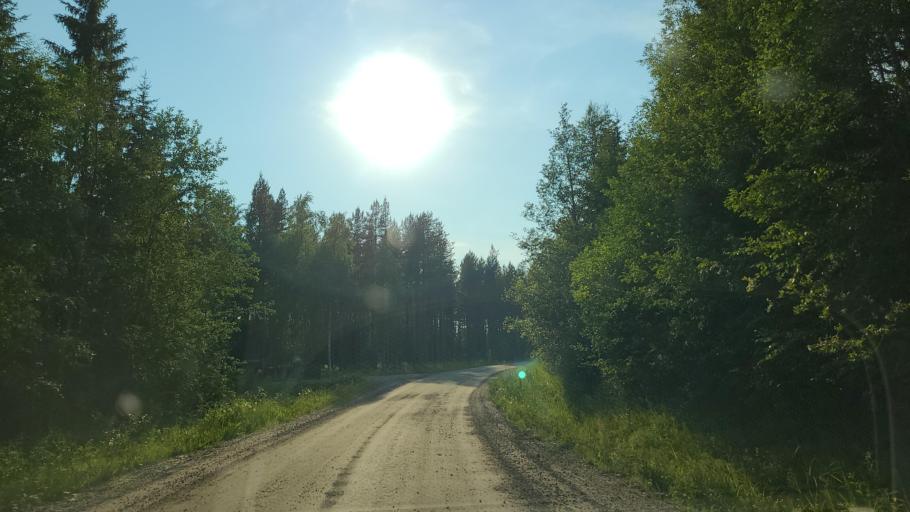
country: SE
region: Vaesterbotten
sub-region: Skelleftea Kommun
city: Burea
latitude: 64.3605
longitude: 21.4146
